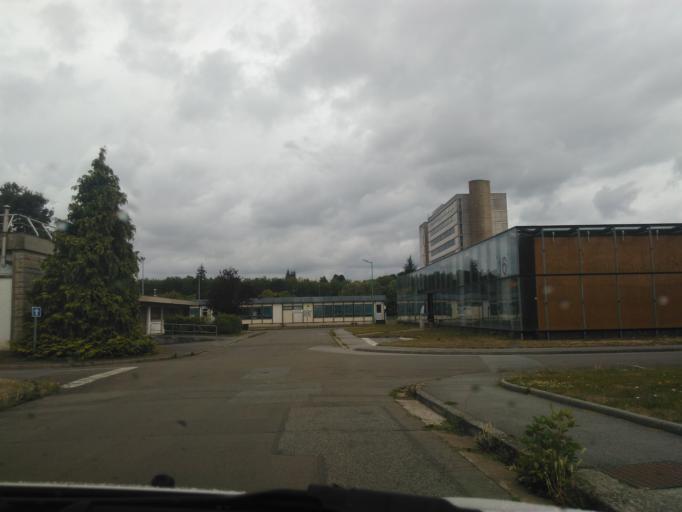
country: FR
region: Brittany
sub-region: Departement d'Ille-et-Vilaine
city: Rennes
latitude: 48.1174
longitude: -1.6416
